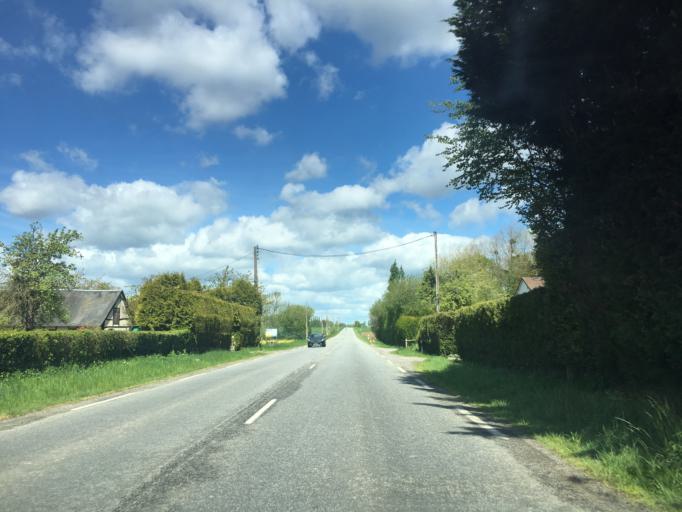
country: FR
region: Lower Normandy
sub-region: Departement de l'Orne
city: Rai
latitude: 48.8182
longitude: 0.5703
